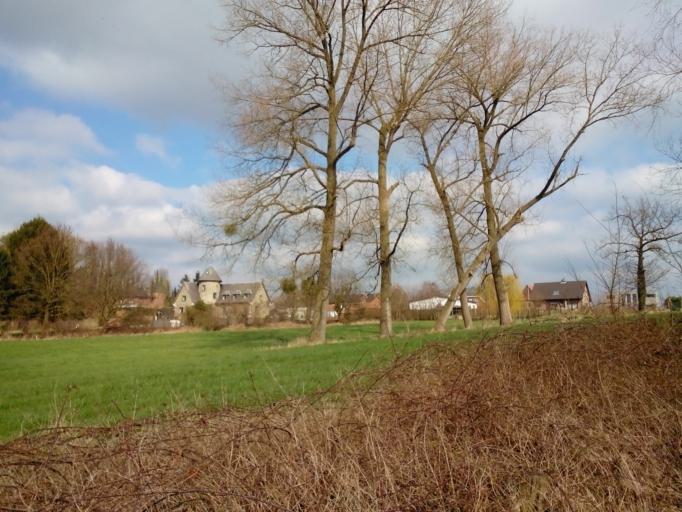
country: BE
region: Flanders
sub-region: Provincie Vlaams-Brabant
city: Boutersem
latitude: 50.8497
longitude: 4.8194
